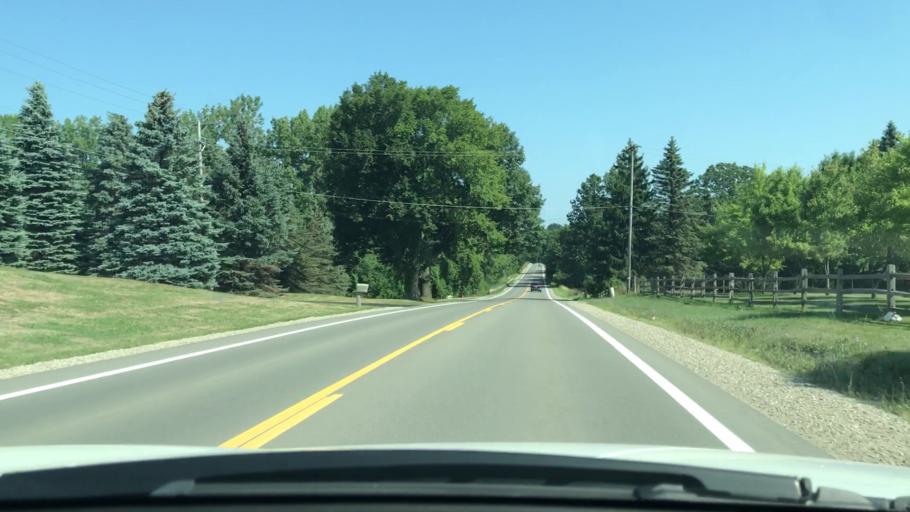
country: US
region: Michigan
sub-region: Oakland County
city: Oxford
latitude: 42.8001
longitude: -83.3332
